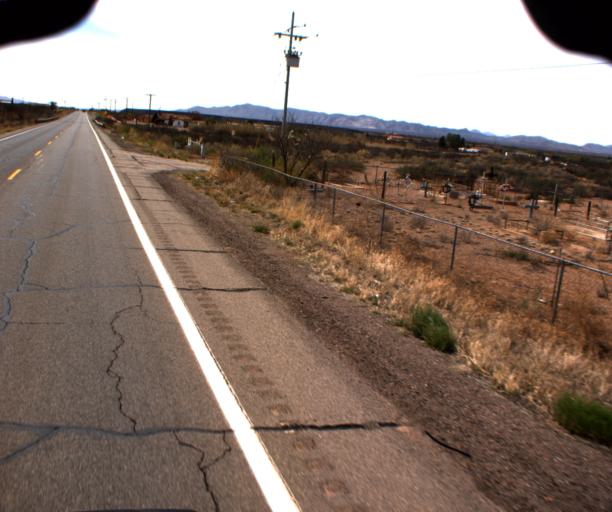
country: US
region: Arizona
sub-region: Cochise County
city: Pirtleville
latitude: 31.3639
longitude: -109.5794
